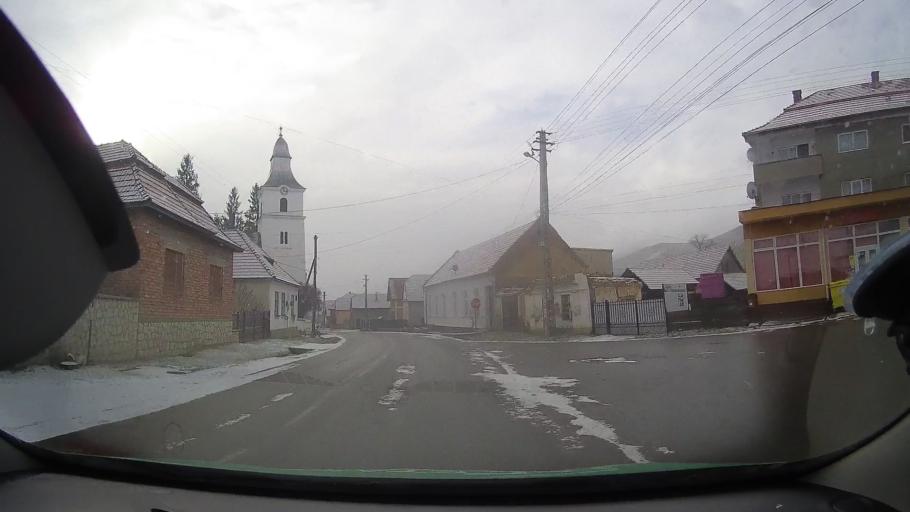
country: RO
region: Alba
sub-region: Comuna Rimetea
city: Rimetea
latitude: 46.4226
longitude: 23.5614
